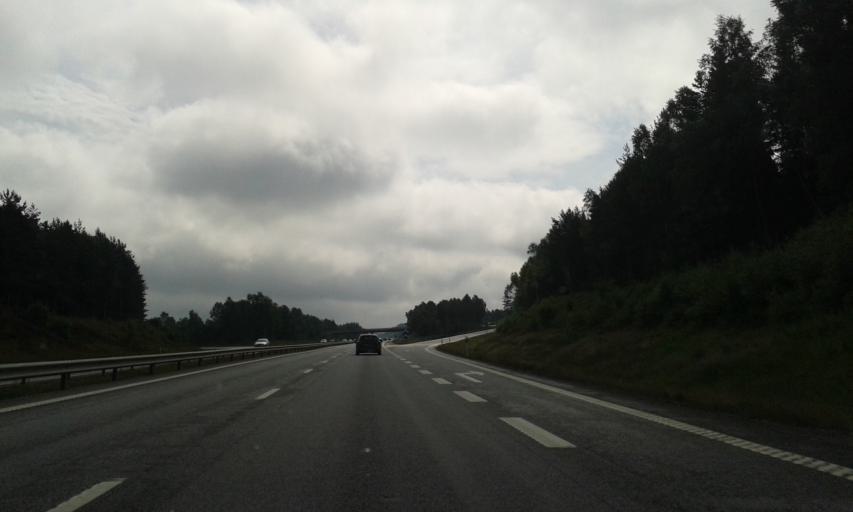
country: SE
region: Vaestra Goetaland
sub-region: Harryda Kommun
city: Hindas
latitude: 57.6764
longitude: 12.3442
